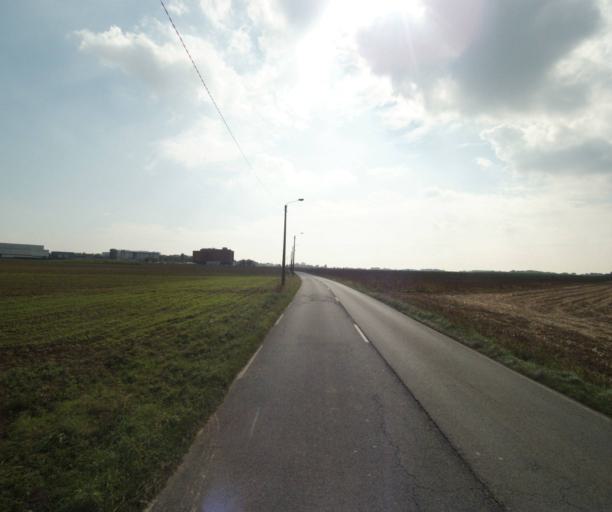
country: FR
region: Nord-Pas-de-Calais
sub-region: Departement du Nord
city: Houplin-Ancoisne
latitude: 50.5720
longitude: 3.0195
